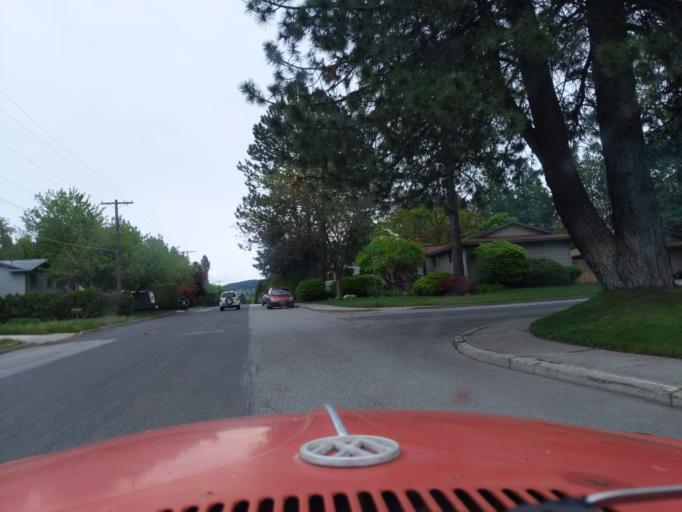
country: US
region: Washington
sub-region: Spokane County
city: Spokane
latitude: 47.5968
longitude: -117.3790
